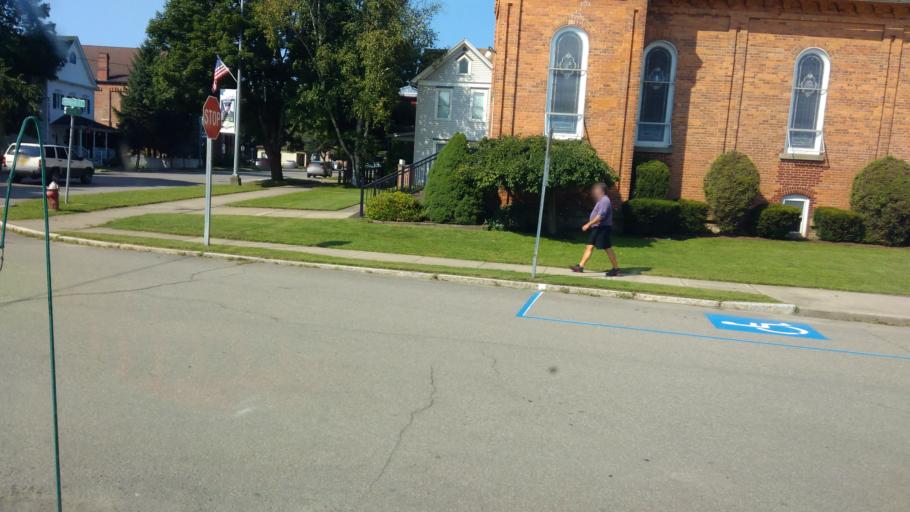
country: US
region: New York
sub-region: Allegany County
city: Cuba
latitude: 42.2182
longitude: -78.2731
